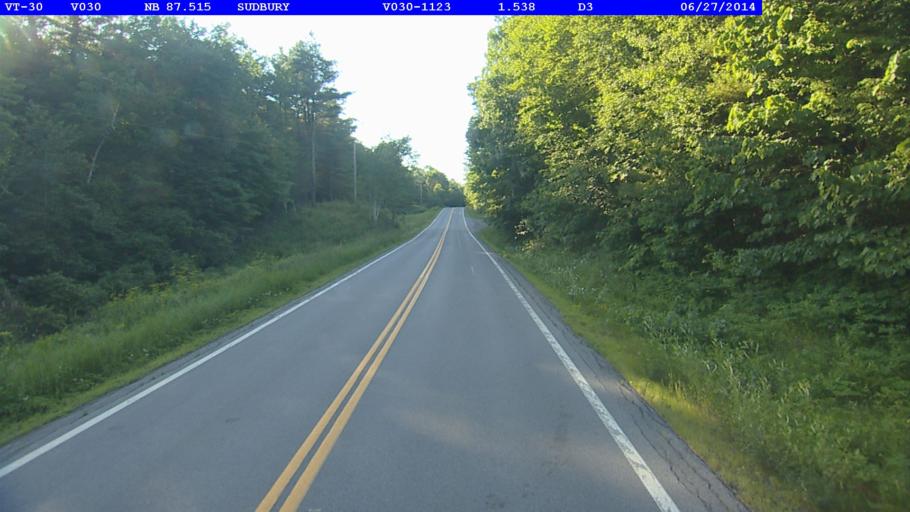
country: US
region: Vermont
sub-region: Rutland County
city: Brandon
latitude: 43.7709
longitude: -73.1996
